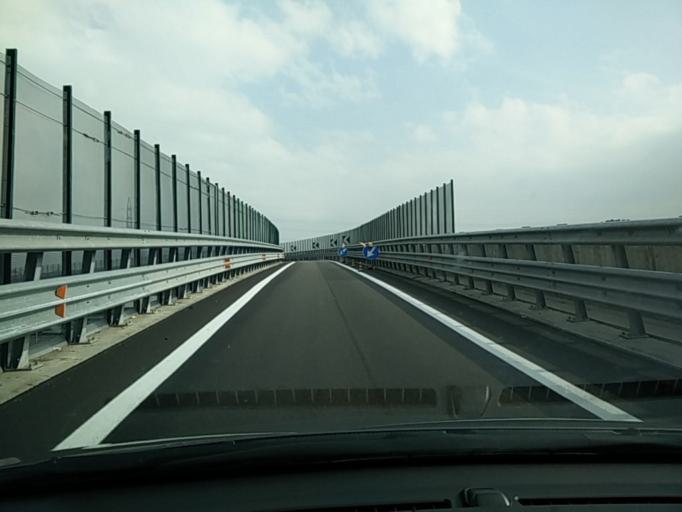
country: IT
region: Lombardy
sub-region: Citta metropolitana di Milano
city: Marcallo
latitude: 45.4898
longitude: 8.8615
